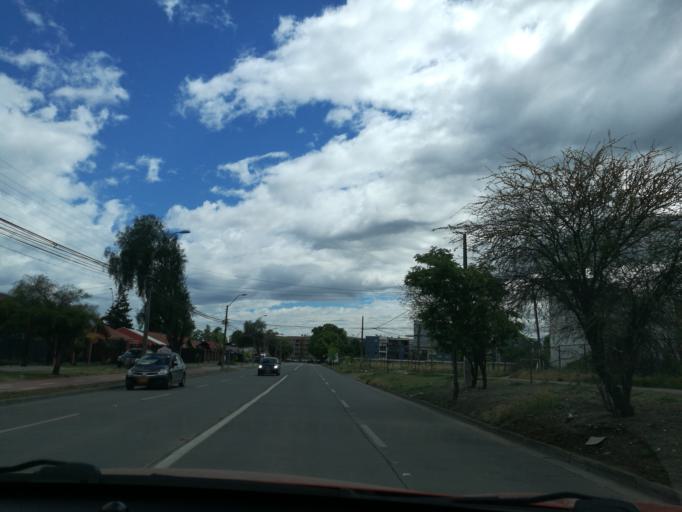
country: CL
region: O'Higgins
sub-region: Provincia de Cachapoal
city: Rancagua
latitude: -34.1426
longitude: -70.7352
